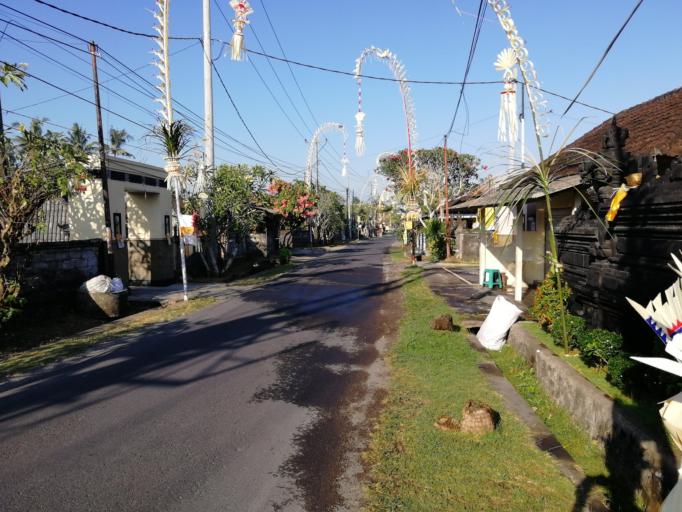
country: ID
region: Bali
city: Banjar Gunungpande
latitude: -8.6274
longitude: 115.1431
